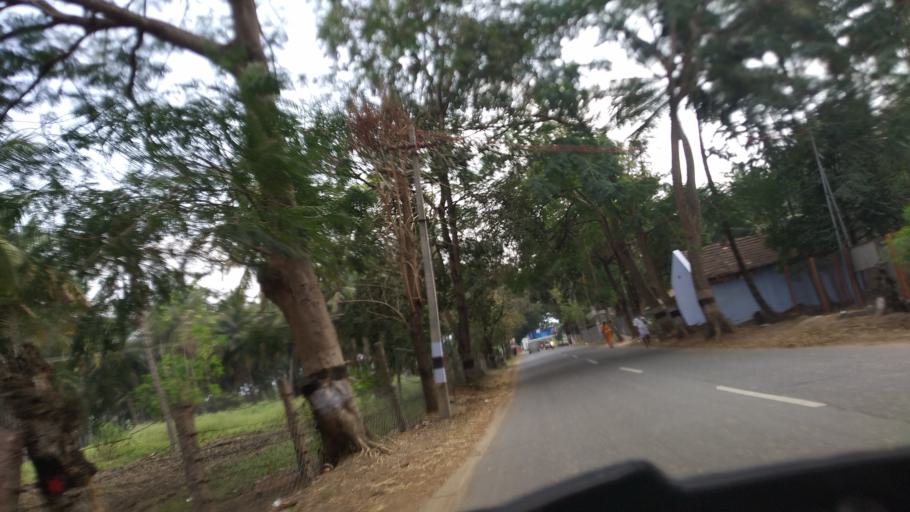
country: IN
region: Tamil Nadu
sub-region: Coimbatore
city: Perur
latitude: 10.9610
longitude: 76.7496
